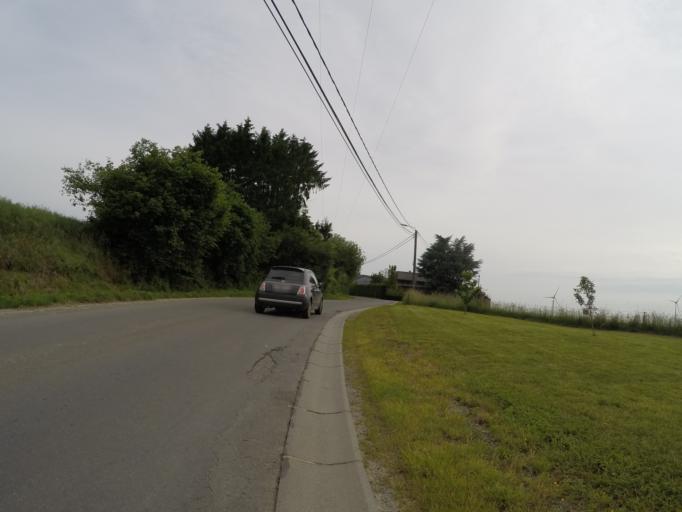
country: BE
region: Wallonia
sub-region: Province de Namur
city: Dinant
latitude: 50.2849
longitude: 4.9654
